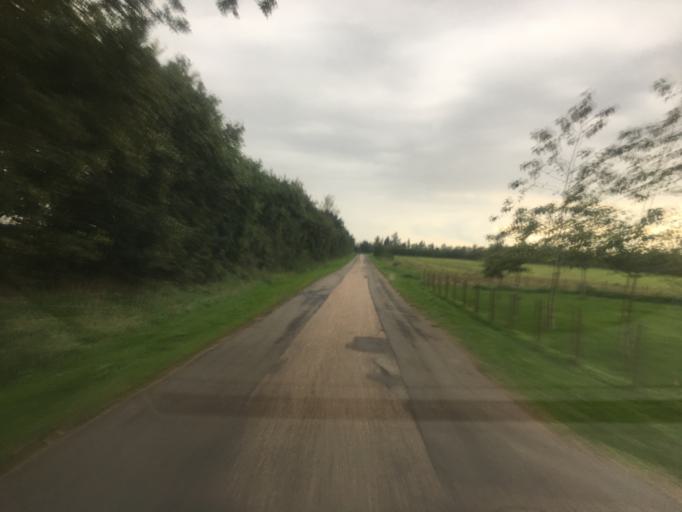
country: DE
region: Schleswig-Holstein
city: Ellhoft
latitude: 54.9578
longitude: 8.9925
